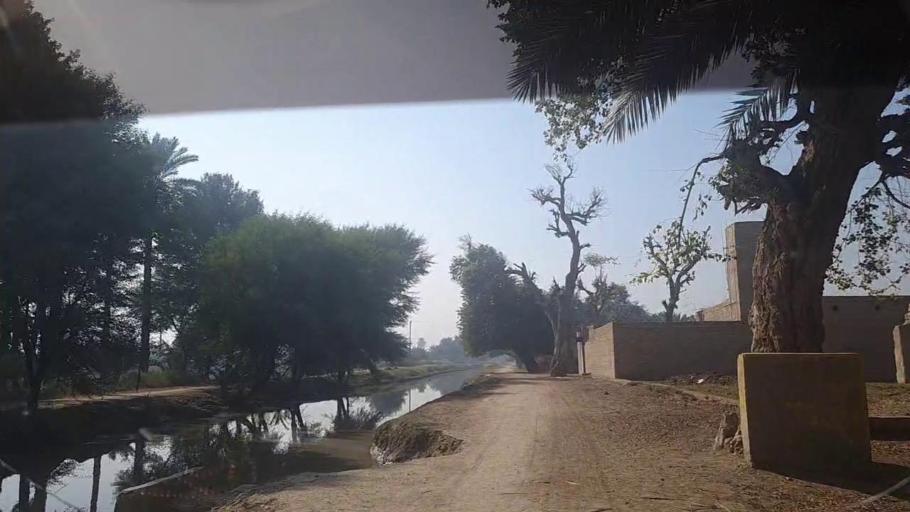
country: PK
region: Sindh
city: Khairpur
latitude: 27.4760
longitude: 68.7288
